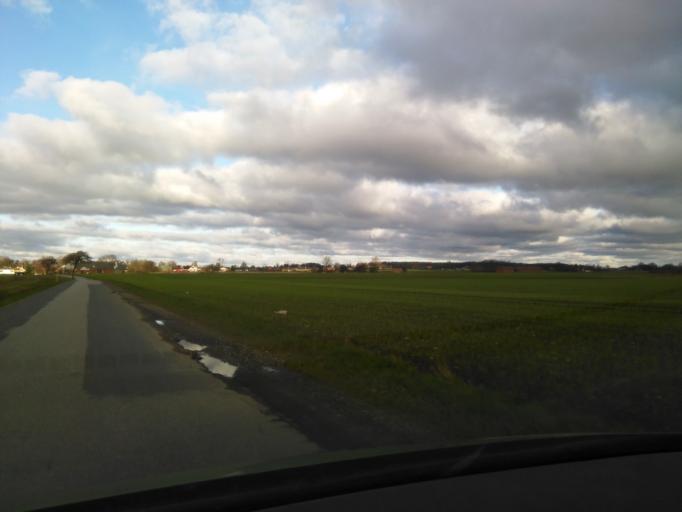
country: DK
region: Central Jutland
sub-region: Odder Kommune
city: Odder
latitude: 55.8835
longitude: 10.1712
